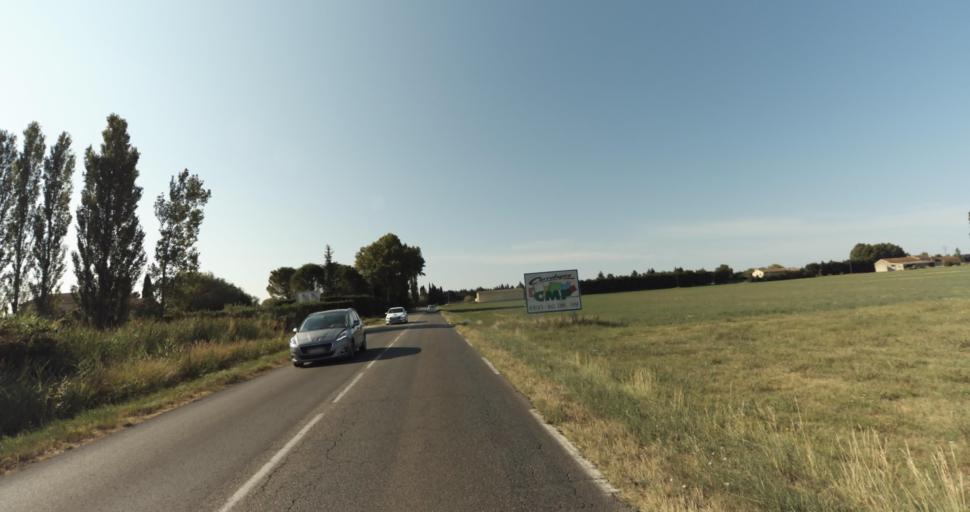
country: FR
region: Provence-Alpes-Cote d'Azur
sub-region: Departement du Vaucluse
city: Monteux
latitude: 44.0559
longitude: 4.9788
